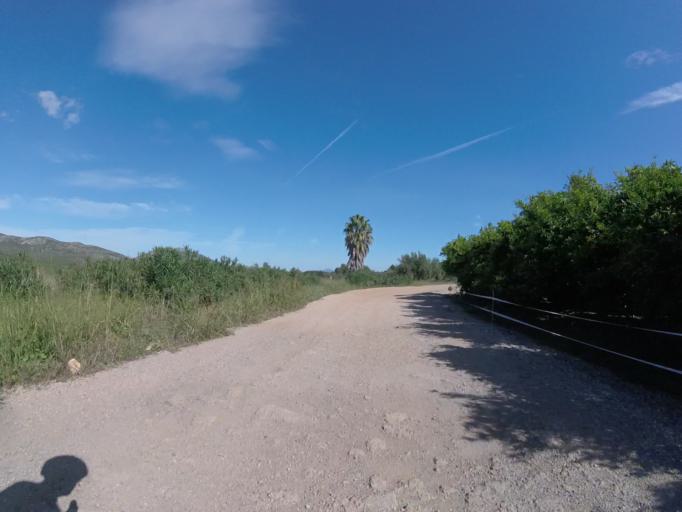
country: ES
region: Valencia
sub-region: Provincia de Castello
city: Santa Magdalena de Pulpis
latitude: 40.3803
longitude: 0.3367
